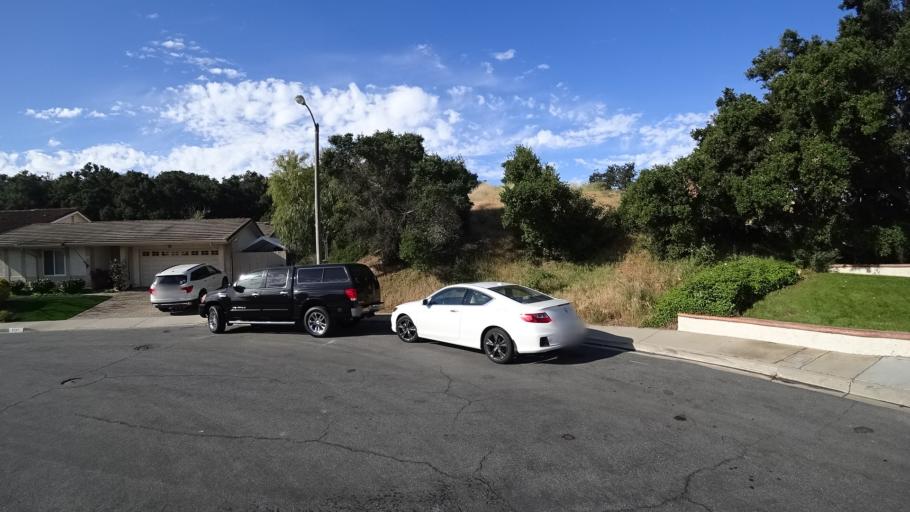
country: US
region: California
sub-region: Ventura County
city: Casa Conejo
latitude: 34.1716
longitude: -118.9447
